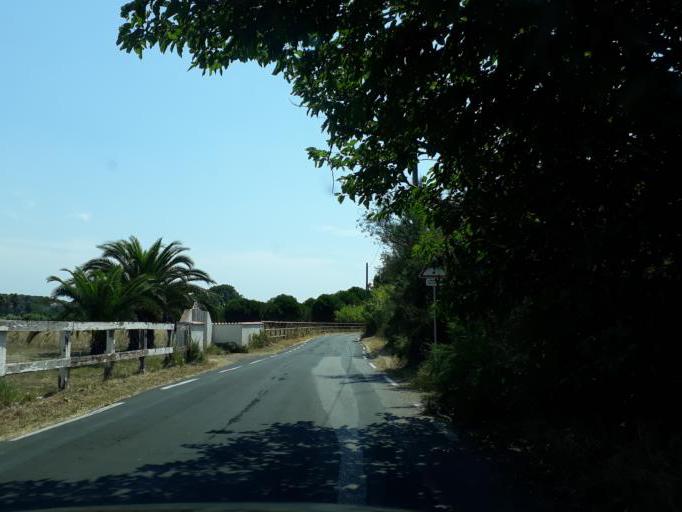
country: FR
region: Languedoc-Roussillon
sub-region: Departement de l'Herault
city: Agde
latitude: 43.2856
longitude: 3.4818
